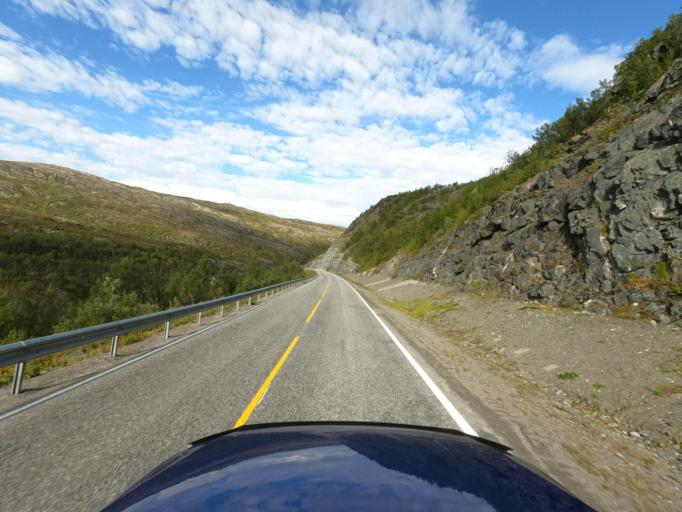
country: NO
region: Finnmark Fylke
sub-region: Kvalsund
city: Kvalsund
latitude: 70.3863
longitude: 24.4498
